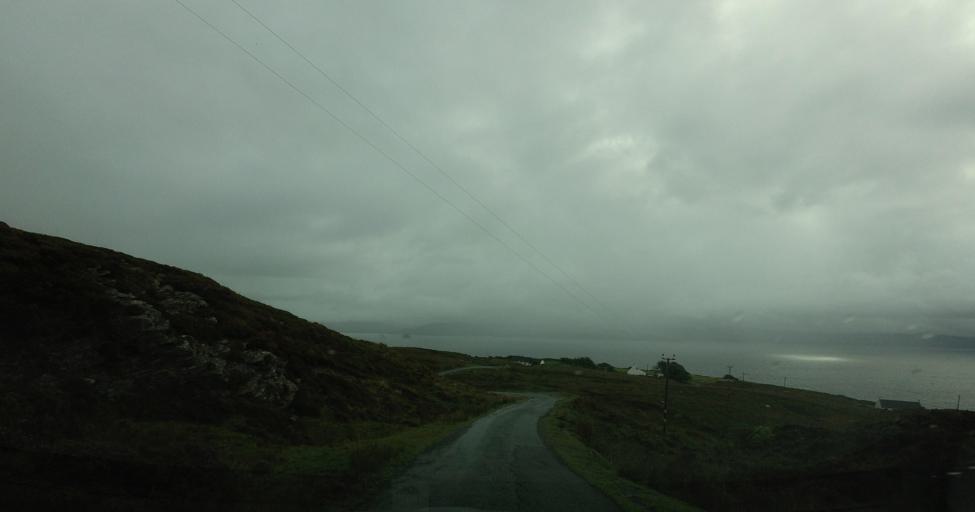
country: GB
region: Scotland
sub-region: Highland
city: Isle of Skye
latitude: 57.1427
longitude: -6.0758
